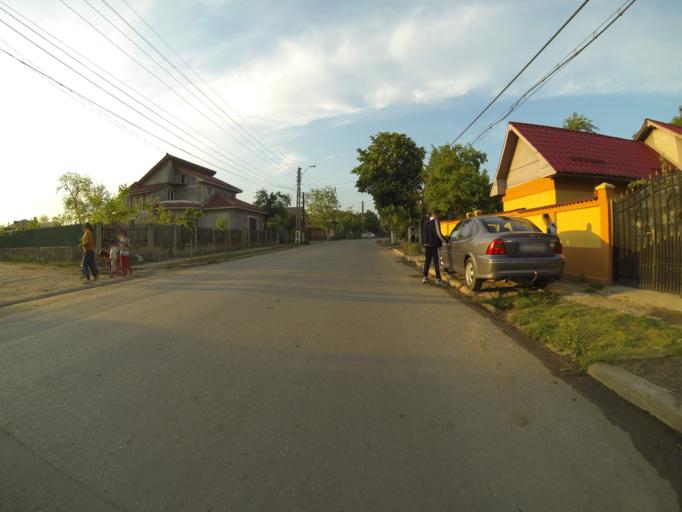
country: RO
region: Dolj
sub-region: Comuna Segarcea
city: Segarcea
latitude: 44.0932
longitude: 23.7354
